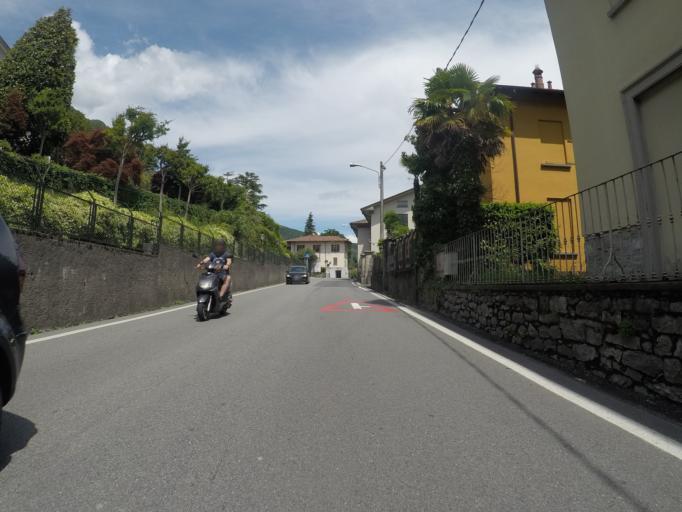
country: IT
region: Lombardy
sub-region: Provincia di Como
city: Lenno
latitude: 45.9748
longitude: 9.1973
